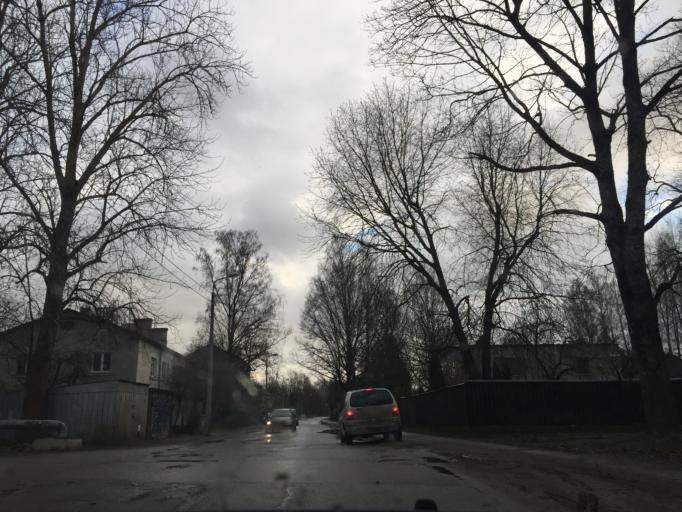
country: LV
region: Marupe
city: Marupe
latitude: 56.9335
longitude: 24.0553
